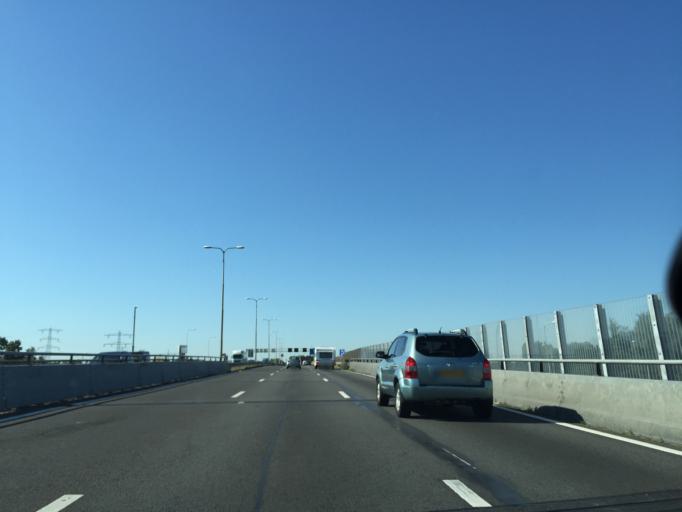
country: NL
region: Limburg
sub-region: Gemeente Stein
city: Urmond
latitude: 50.9910
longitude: 5.7848
